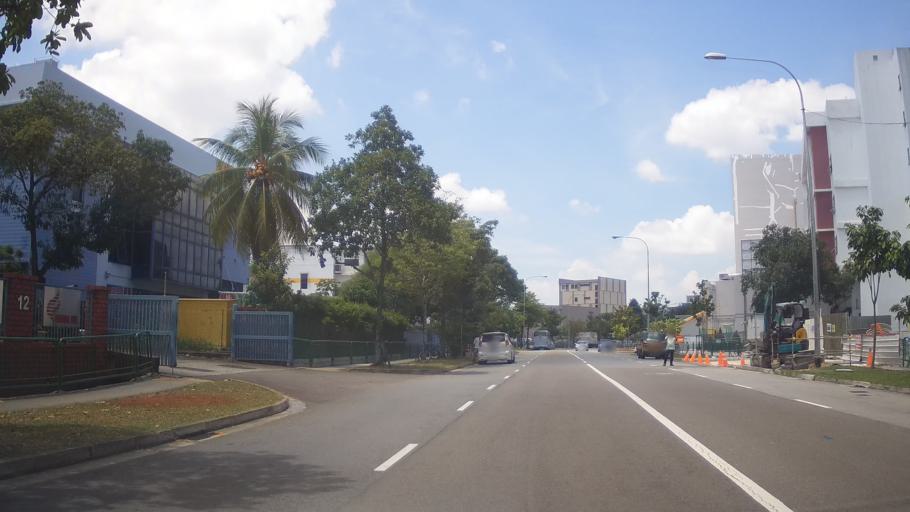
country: MY
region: Johor
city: Johor Bahru
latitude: 1.3361
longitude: 103.7141
